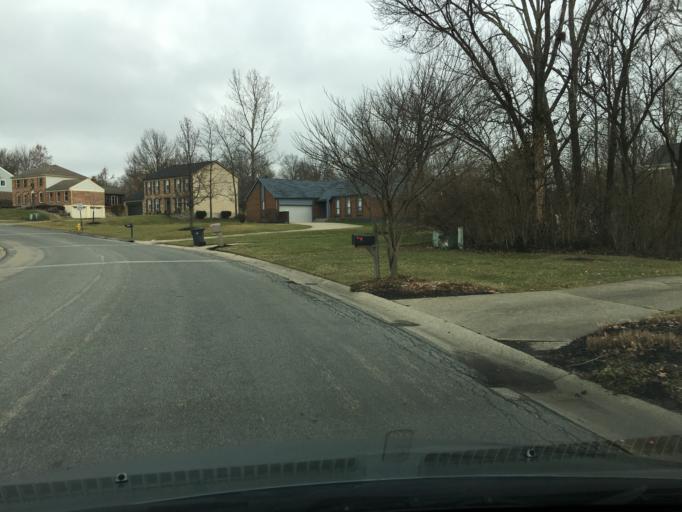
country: US
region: Ohio
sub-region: Hamilton County
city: Sharonville
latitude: 39.3094
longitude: -84.3987
